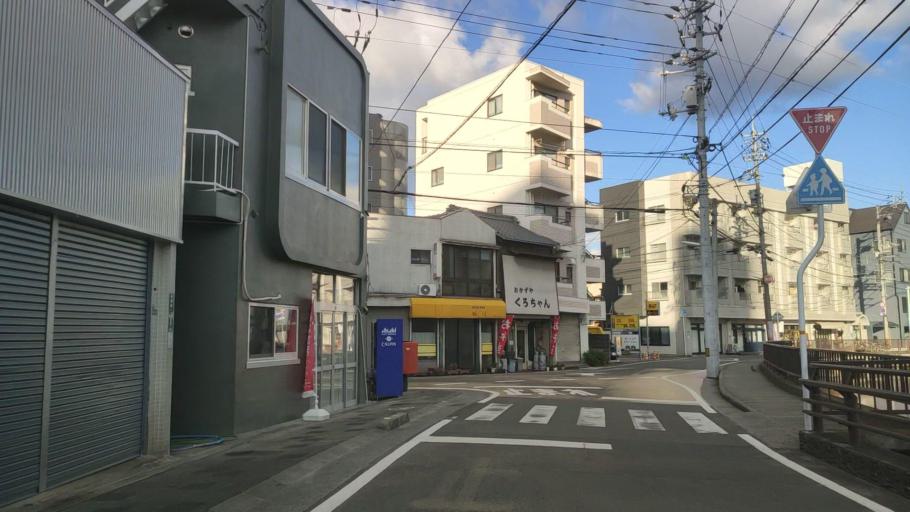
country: JP
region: Ehime
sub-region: Shikoku-chuo Shi
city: Matsuyama
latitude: 33.8471
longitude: 132.7856
